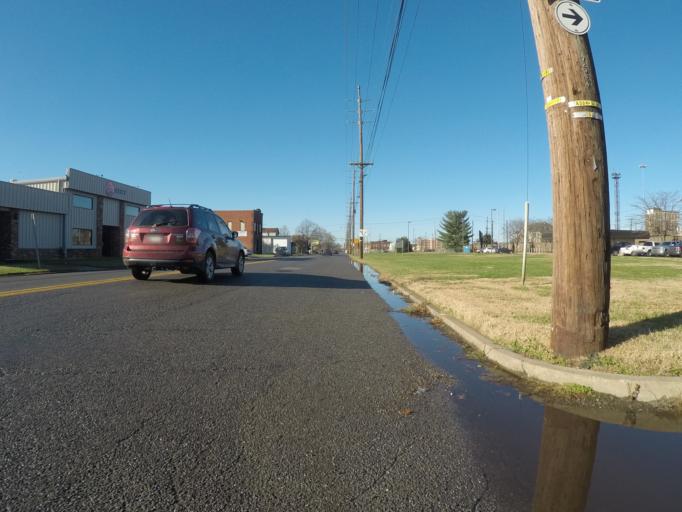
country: US
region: West Virginia
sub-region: Cabell County
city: Huntington
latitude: 38.4157
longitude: -82.4389
